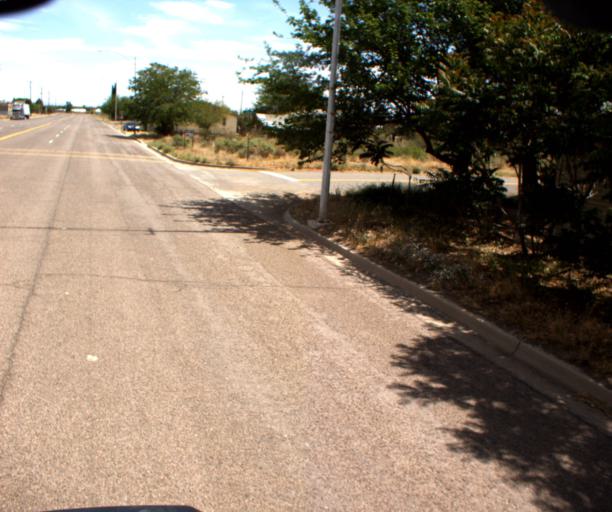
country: US
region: Arizona
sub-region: Cochise County
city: Willcox
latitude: 32.3265
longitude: -109.4885
